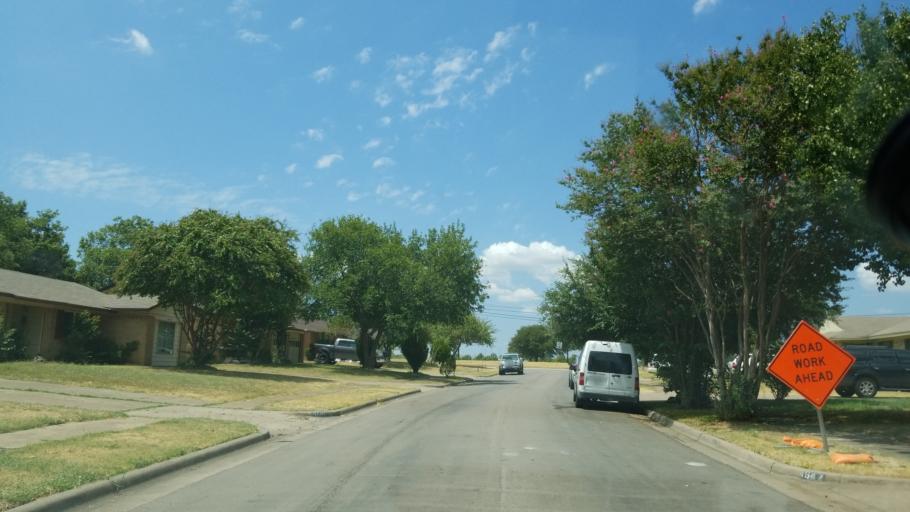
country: US
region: Texas
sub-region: Dallas County
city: Cockrell Hill
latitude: 32.7228
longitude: -96.8992
